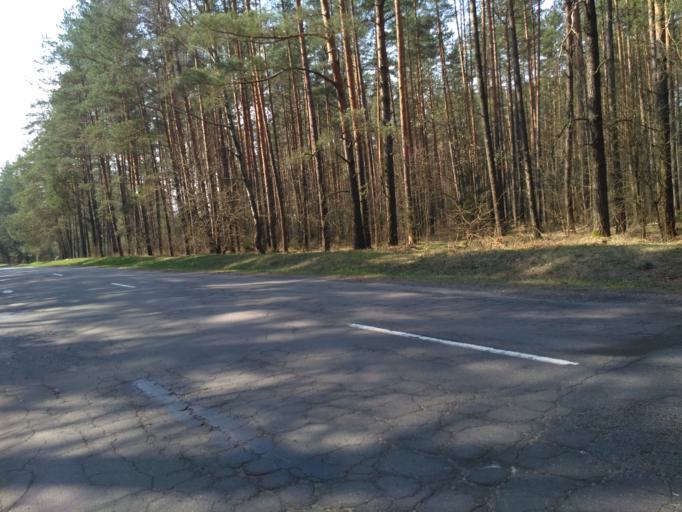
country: BY
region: Minsk
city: Zamostochcha
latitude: 53.8987
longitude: 27.9288
